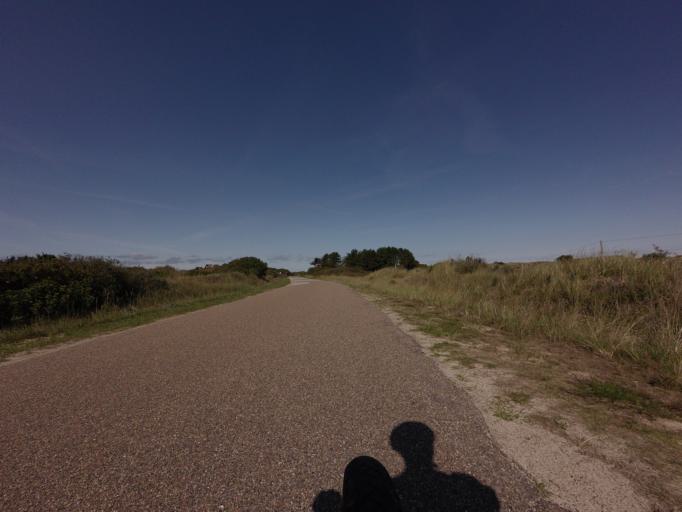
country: DK
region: North Denmark
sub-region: Hjorring Kommune
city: Hirtshals
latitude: 57.5870
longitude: 10.0285
